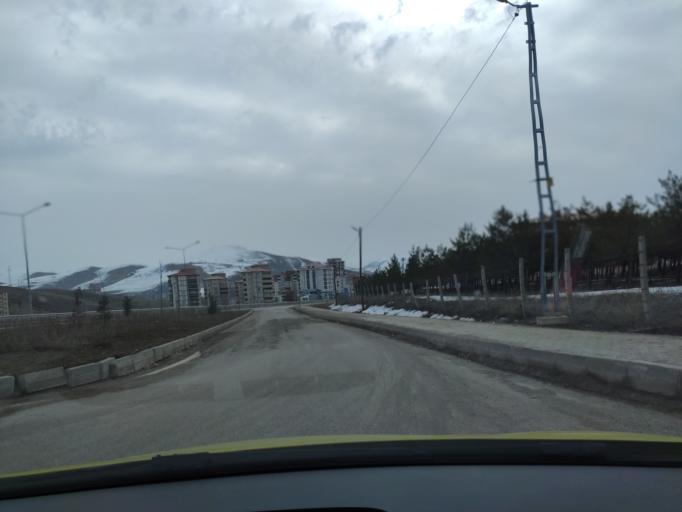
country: TR
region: Bayburt
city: Bayburt
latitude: 40.2719
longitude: 40.1926
